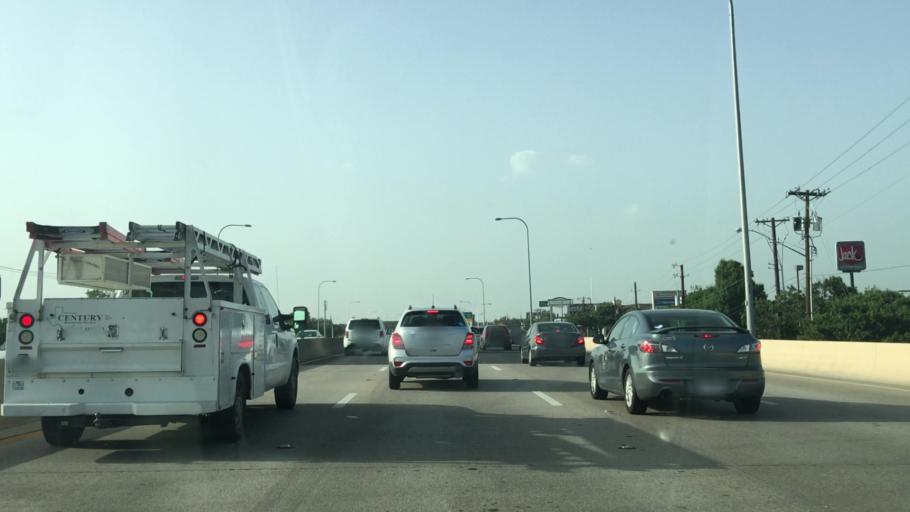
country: US
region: Texas
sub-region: Dallas County
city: Addison
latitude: 32.9980
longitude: -96.8313
